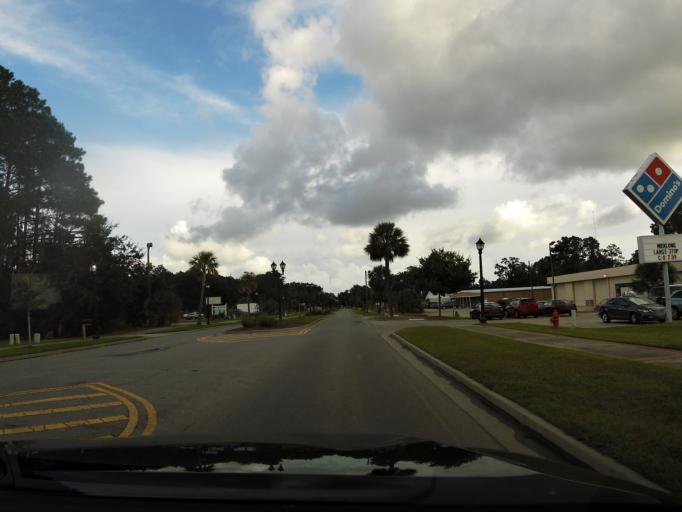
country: US
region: Georgia
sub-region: Liberty County
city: Hinesville
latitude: 31.8539
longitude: -81.6027
